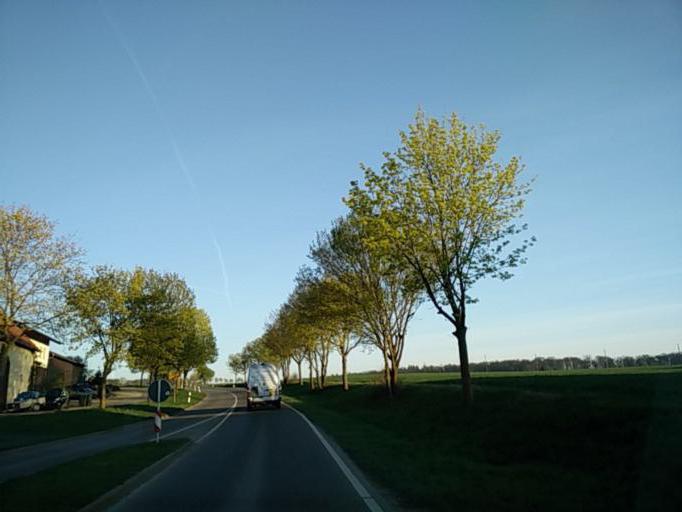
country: DE
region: Baden-Wuerttemberg
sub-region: Regierungsbezirk Stuttgart
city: Hildrizhausen
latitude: 48.6272
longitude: 8.9630
